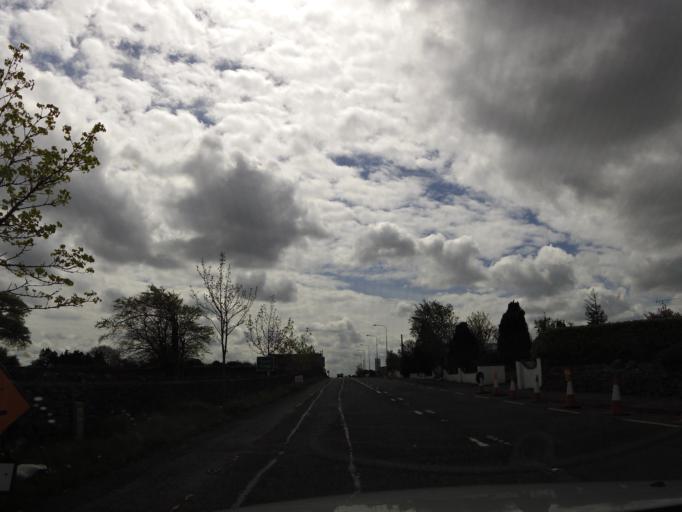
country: IE
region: Connaught
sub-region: County Galway
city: Tuam
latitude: 53.5329
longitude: -8.8474
